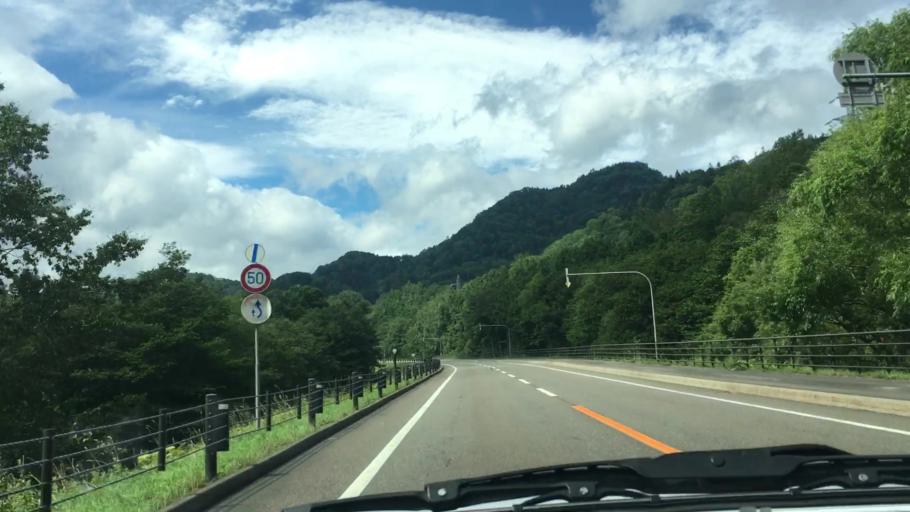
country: JP
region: Hokkaido
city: Otofuke
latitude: 43.3647
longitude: 143.2349
